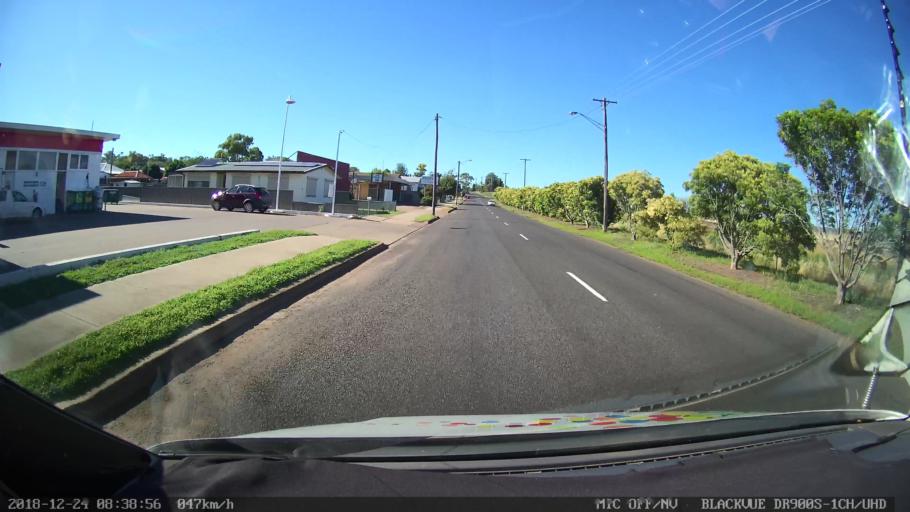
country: AU
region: New South Wales
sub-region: Liverpool Plains
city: Quirindi
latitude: -31.3445
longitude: 150.6475
